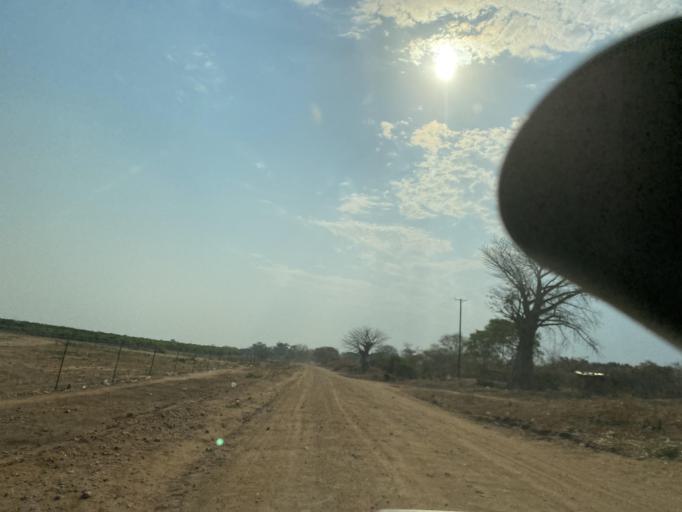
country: ZW
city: Chirundu
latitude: -15.9311
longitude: 28.9559
